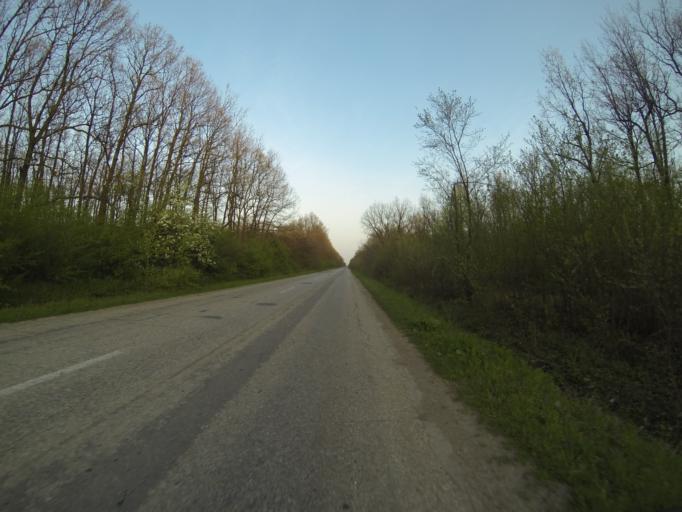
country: RO
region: Dolj
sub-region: Comuna Dranicu
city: Dranic
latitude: 44.0670
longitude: 23.8055
